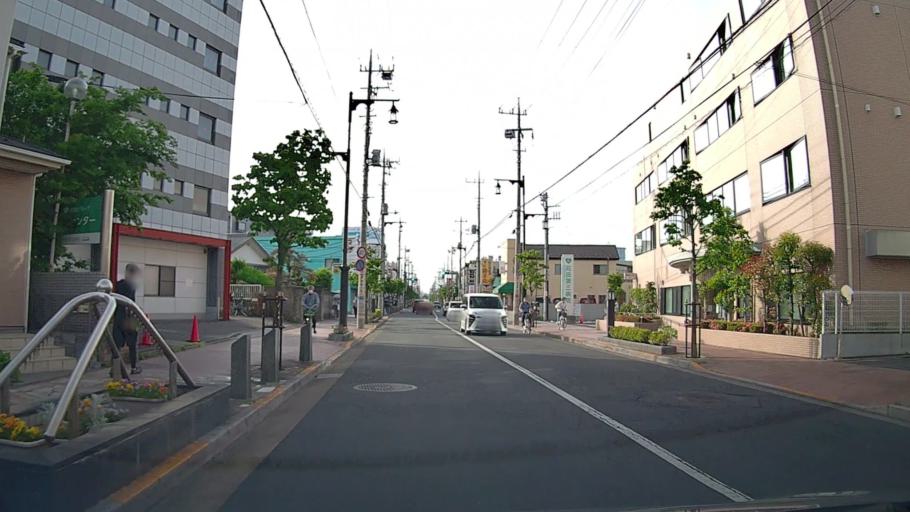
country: JP
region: Saitama
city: Soka
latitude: 35.8000
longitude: 139.7849
